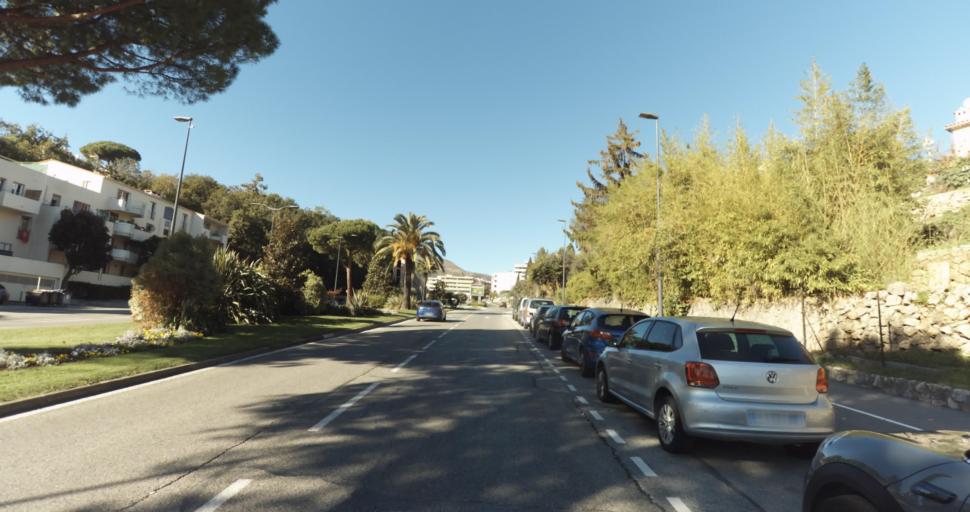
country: FR
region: Provence-Alpes-Cote d'Azur
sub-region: Departement des Alpes-Maritimes
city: Vence
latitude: 43.7200
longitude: 7.1123
